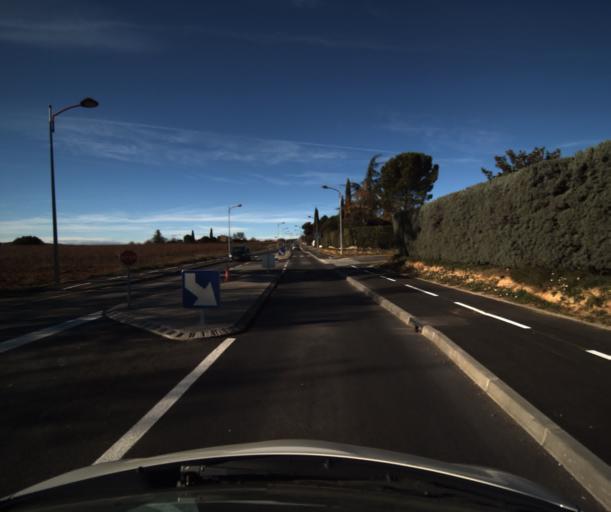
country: FR
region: Provence-Alpes-Cote d'Azur
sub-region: Departement du Vaucluse
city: Pertuis
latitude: 43.6967
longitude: 5.4825
